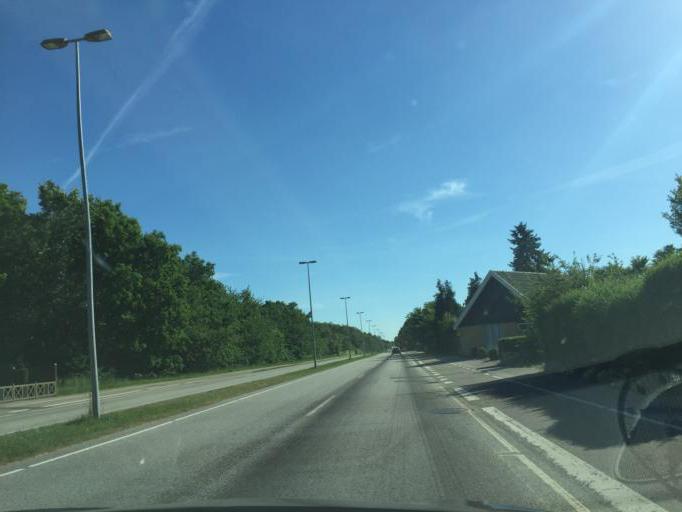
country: DK
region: Zealand
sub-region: Koge Kommune
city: Koge
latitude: 55.4102
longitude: 12.1337
